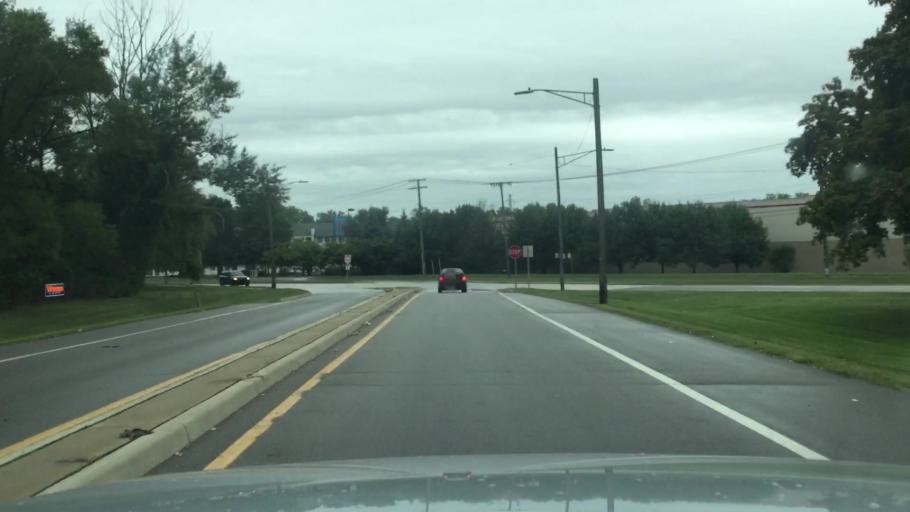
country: US
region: Michigan
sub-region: Macomb County
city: Center Line
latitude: 42.5242
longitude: -83.0274
